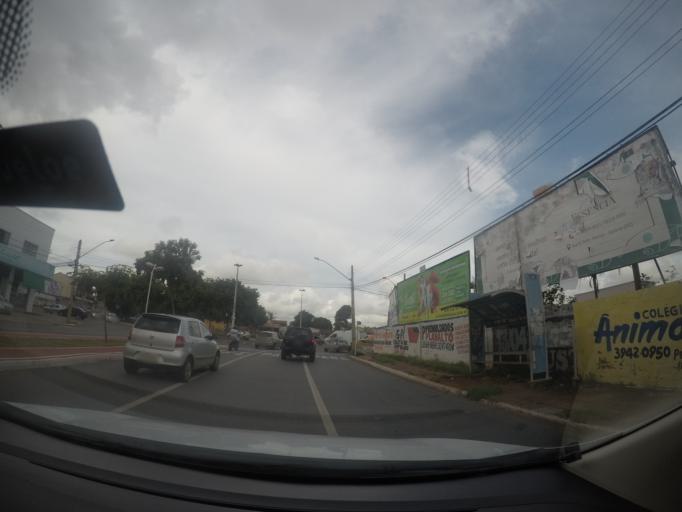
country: BR
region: Goias
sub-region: Goiania
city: Goiania
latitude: -16.7211
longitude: -49.3030
